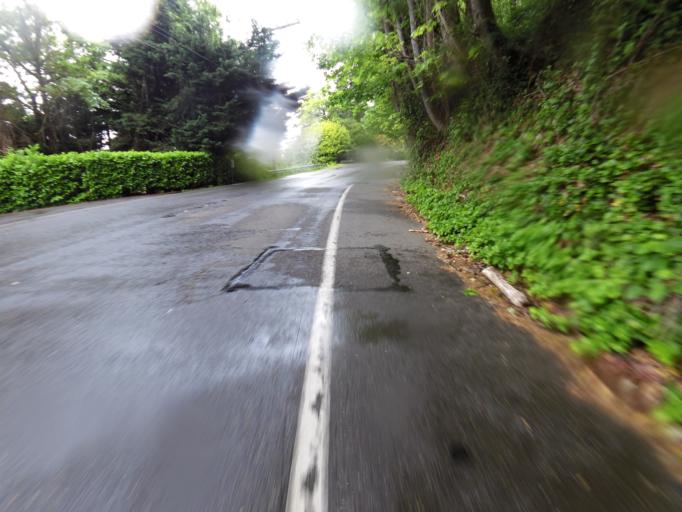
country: US
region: Washington
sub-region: King County
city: Bryn Mawr-Skyway
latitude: 47.5267
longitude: -122.2286
